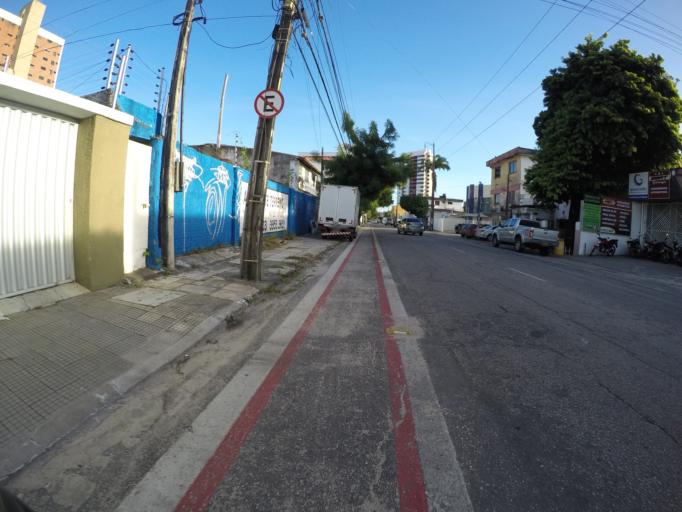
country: BR
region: Ceara
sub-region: Fortaleza
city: Fortaleza
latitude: -3.7445
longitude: -38.5122
